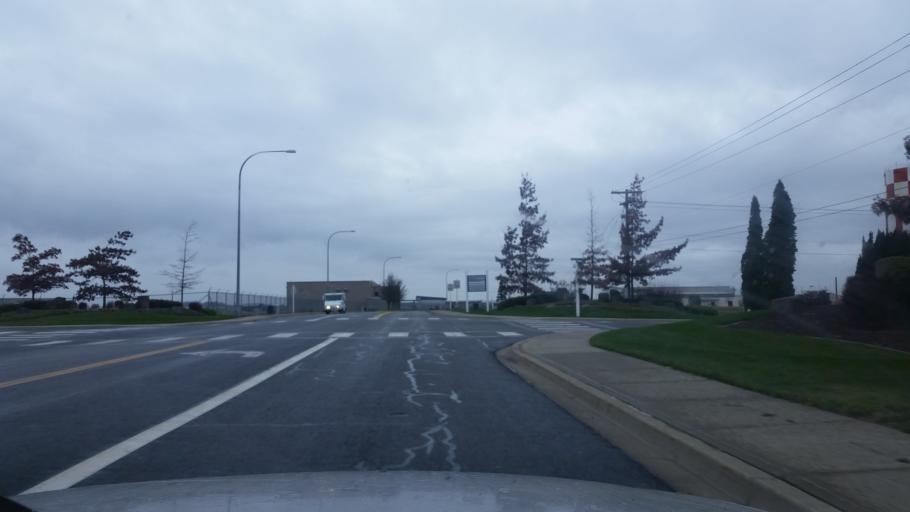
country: US
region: Washington
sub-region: Spokane County
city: Airway Heights
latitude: 47.6191
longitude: -117.5178
